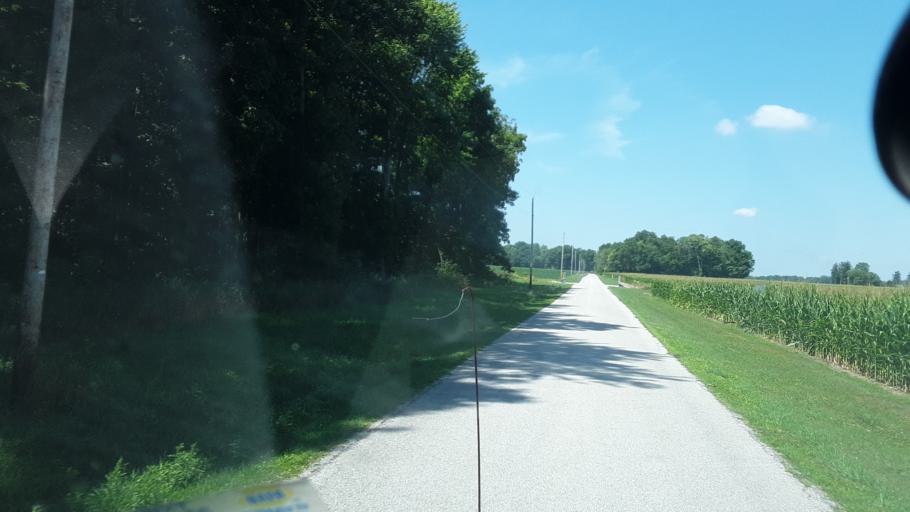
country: US
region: Ohio
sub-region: Hancock County
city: Findlay
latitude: 40.9923
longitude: -83.5281
